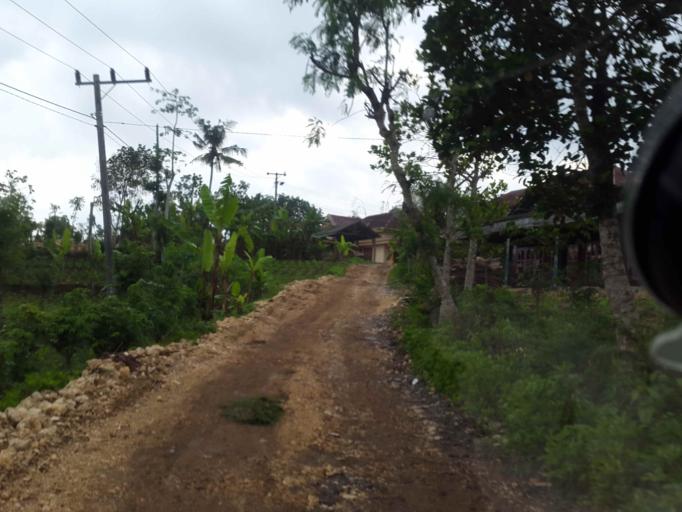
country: ID
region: East Java
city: Tumpakjoho
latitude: -8.1896
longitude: 111.9177
